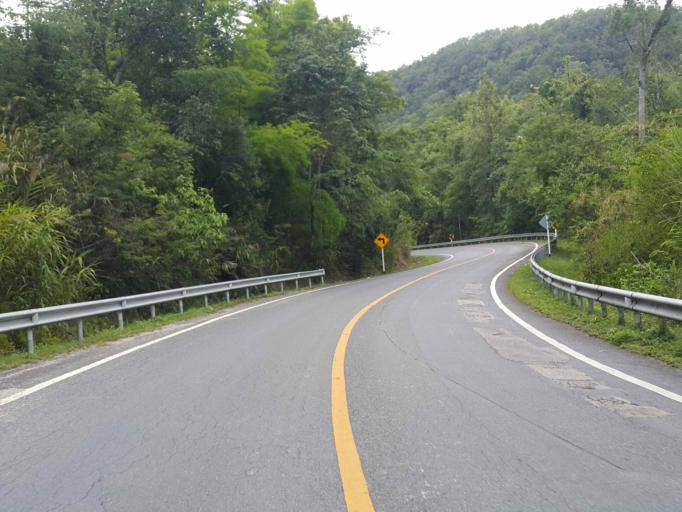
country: TH
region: Chiang Mai
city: Chom Thong
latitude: 18.5286
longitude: 98.6257
